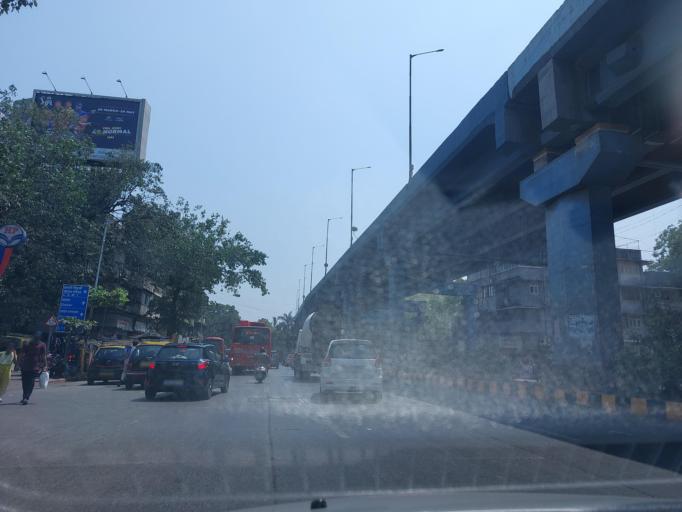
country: IN
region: Maharashtra
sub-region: Mumbai Suburban
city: Mumbai
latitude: 19.0441
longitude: 72.8645
